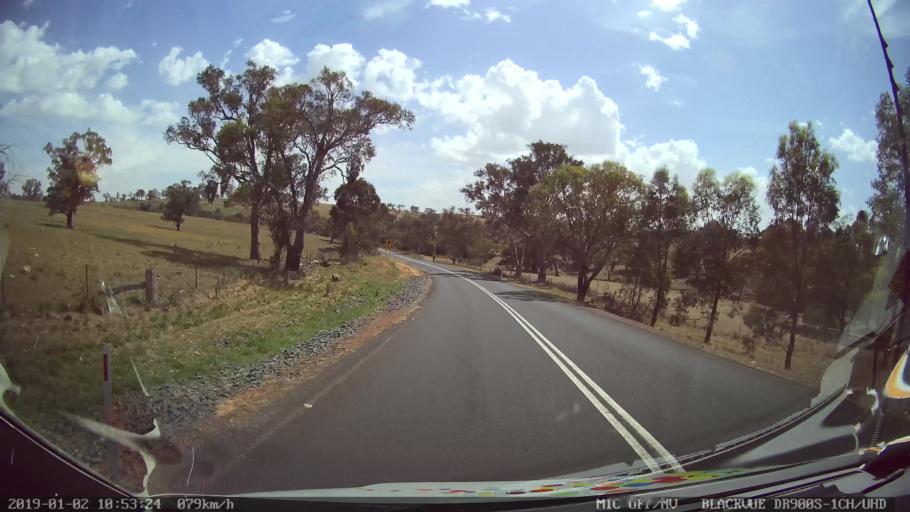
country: AU
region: New South Wales
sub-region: Cootamundra
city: Cootamundra
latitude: -34.6787
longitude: 148.2757
